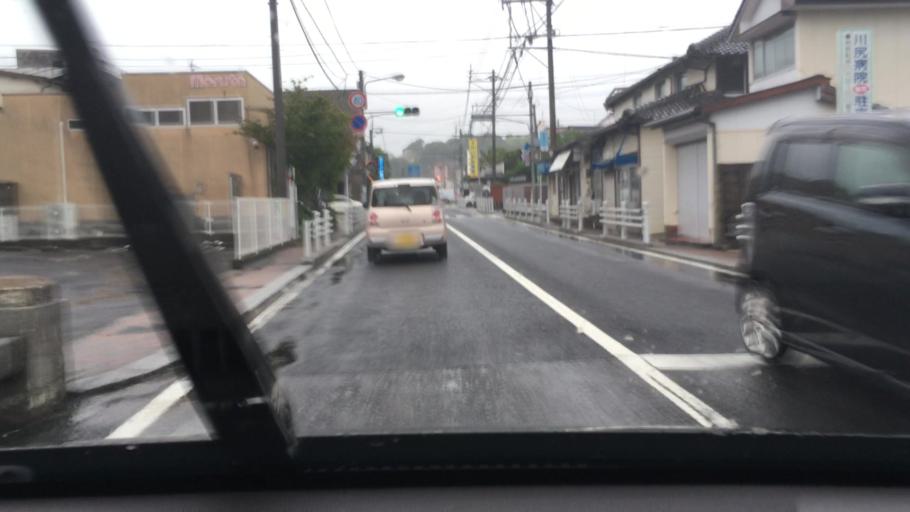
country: JP
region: Nagasaki
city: Sasebo
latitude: 33.1374
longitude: 129.7968
